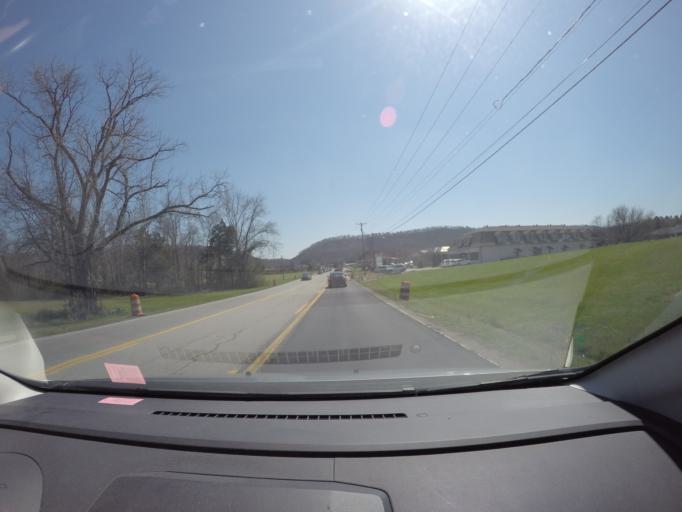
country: US
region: Tennessee
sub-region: Hamilton County
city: Collegedale
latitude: 35.0622
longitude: -85.0726
